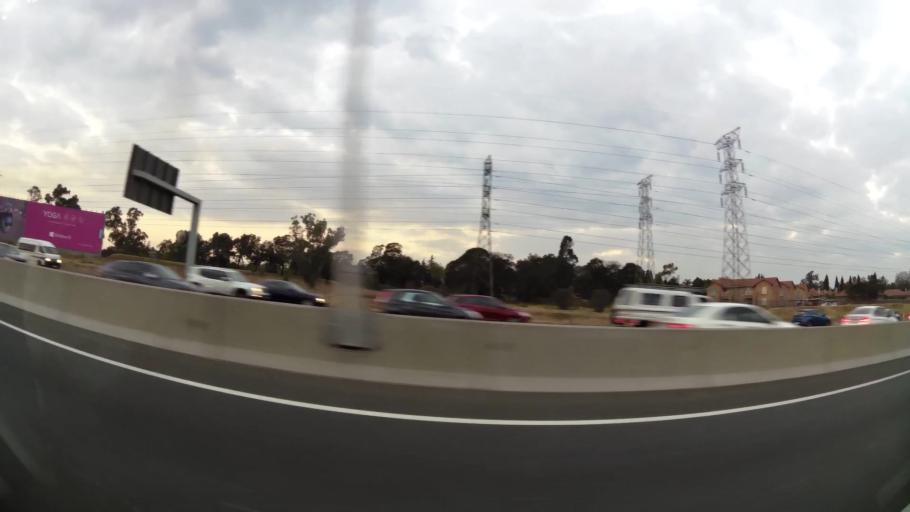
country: ZA
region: Gauteng
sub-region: City of Johannesburg Metropolitan Municipality
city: Modderfontein
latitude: -26.1549
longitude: 28.1325
